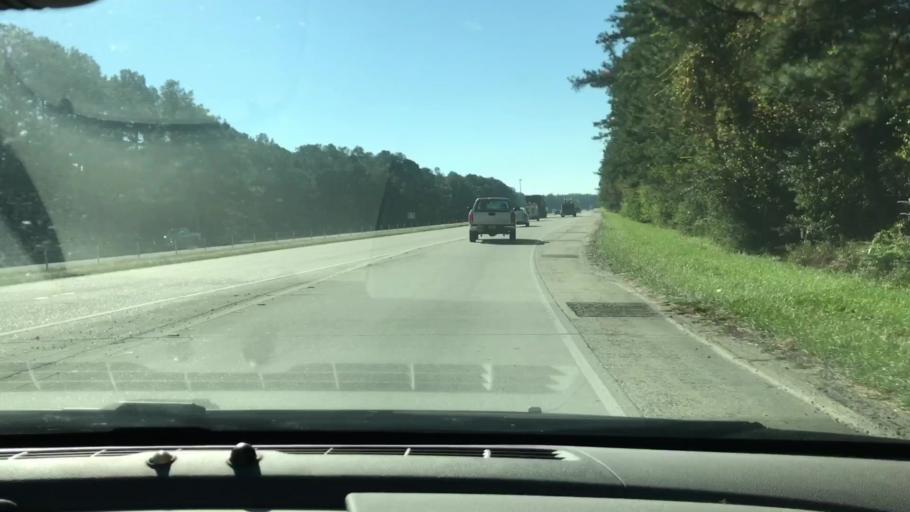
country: US
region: Louisiana
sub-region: Saint Tammany Parish
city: Pearl River
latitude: 30.3519
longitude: -89.7406
